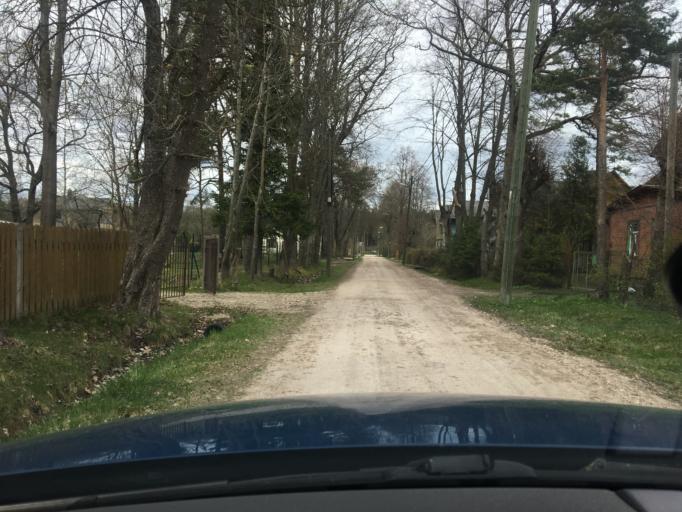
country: LV
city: Tireli
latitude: 56.9477
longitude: 23.4874
